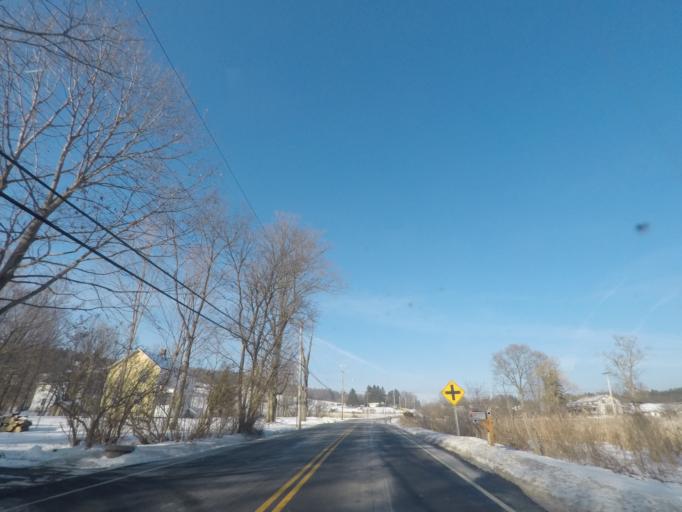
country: US
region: Massachusetts
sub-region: Berkshire County
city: Richmond
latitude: 42.4714
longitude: -73.3920
